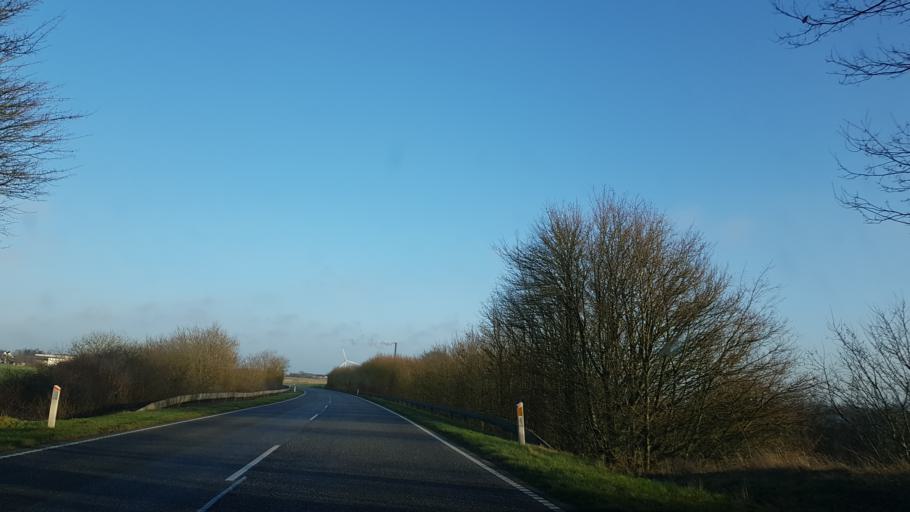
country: DK
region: South Denmark
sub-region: Haderslev Kommune
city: Haderslev
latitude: 55.1993
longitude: 9.4391
